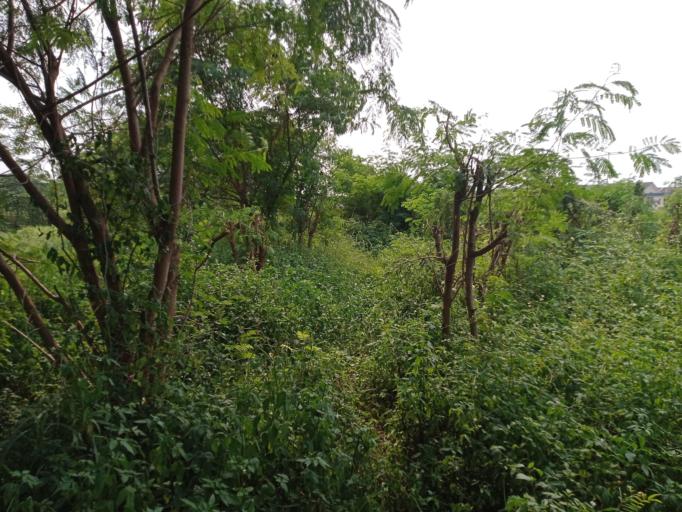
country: ID
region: West Java
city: Pasarkemis
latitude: -6.1536
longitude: 106.5600
